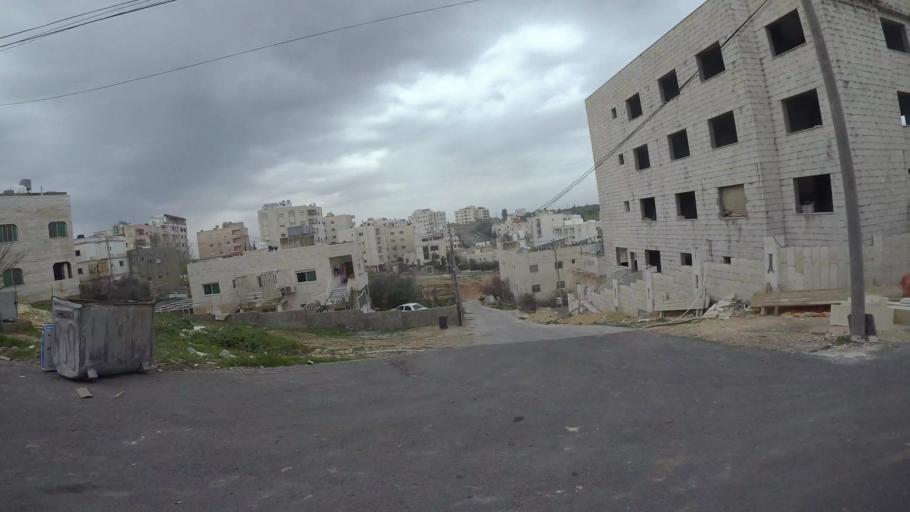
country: JO
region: Amman
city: Umm as Summaq
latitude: 31.9115
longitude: 35.8444
